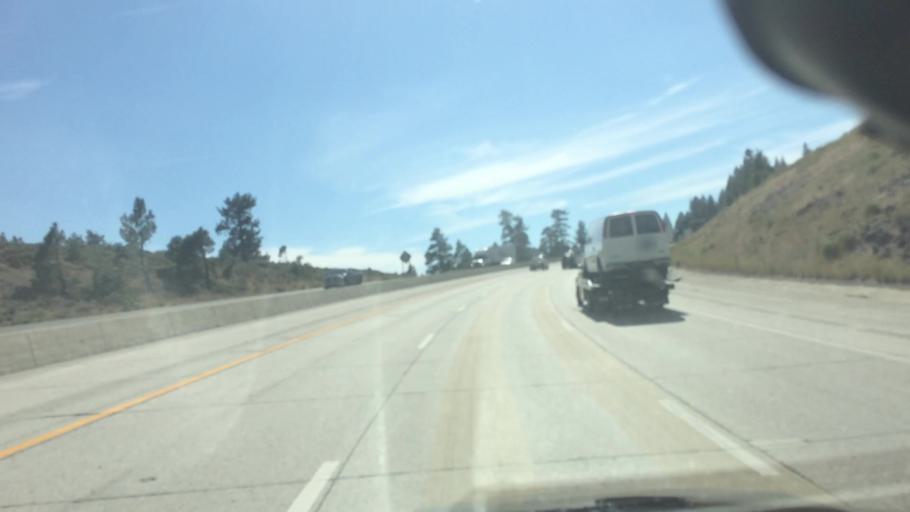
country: US
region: California
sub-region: Nevada County
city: Truckee
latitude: 39.3642
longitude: -120.1184
